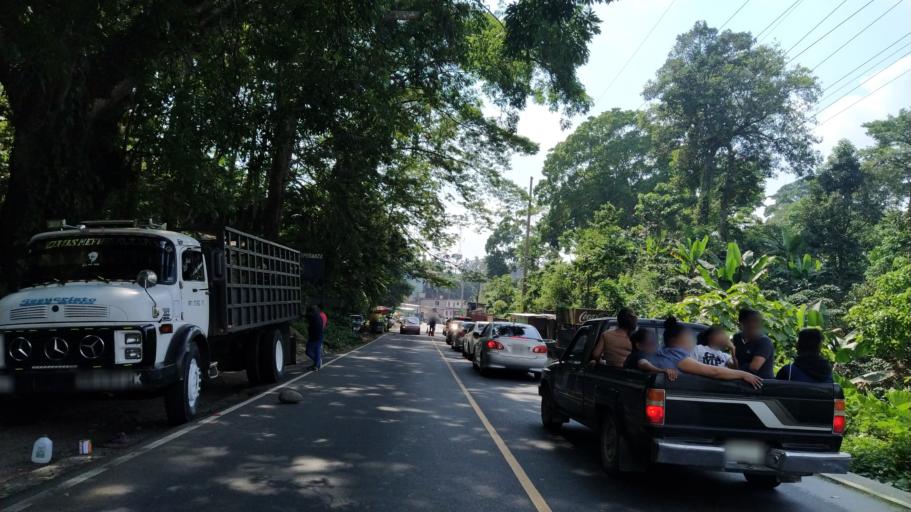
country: GT
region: Quetzaltenango
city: El Palmar
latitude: 14.6370
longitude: -91.5764
